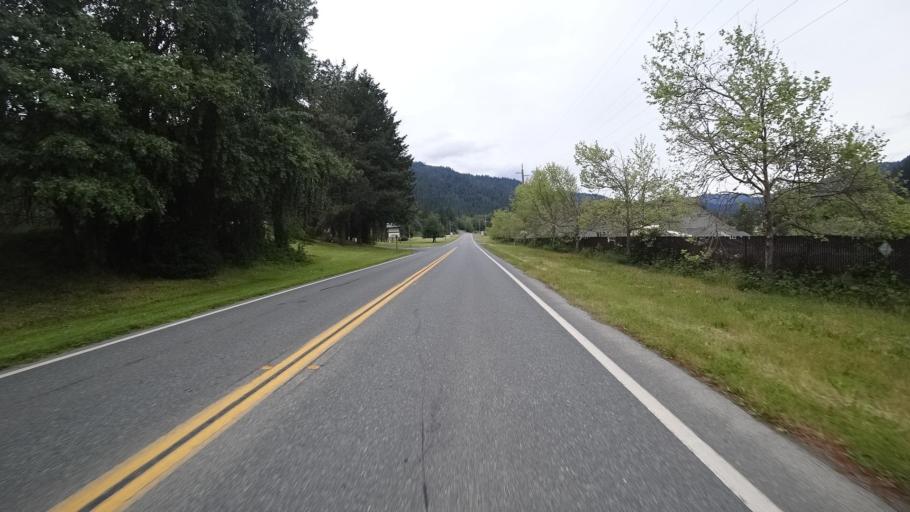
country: US
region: California
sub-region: Humboldt County
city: Willow Creek
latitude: 40.9482
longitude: -123.6370
